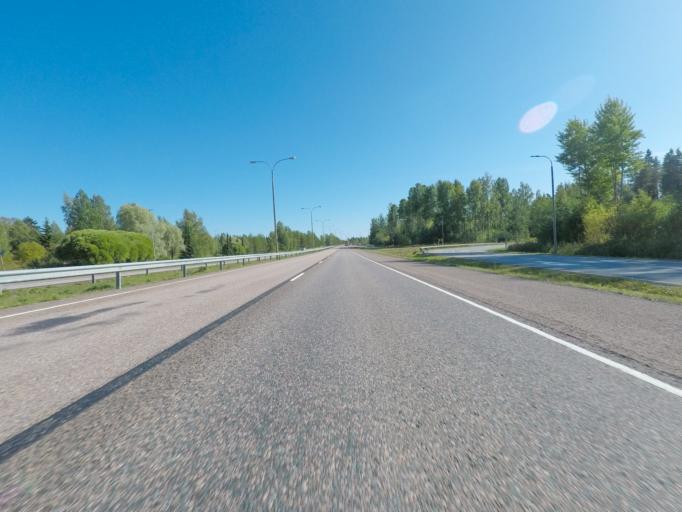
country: FI
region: Northern Savo
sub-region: Varkaus
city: Varkaus
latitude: 62.3178
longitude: 27.8466
